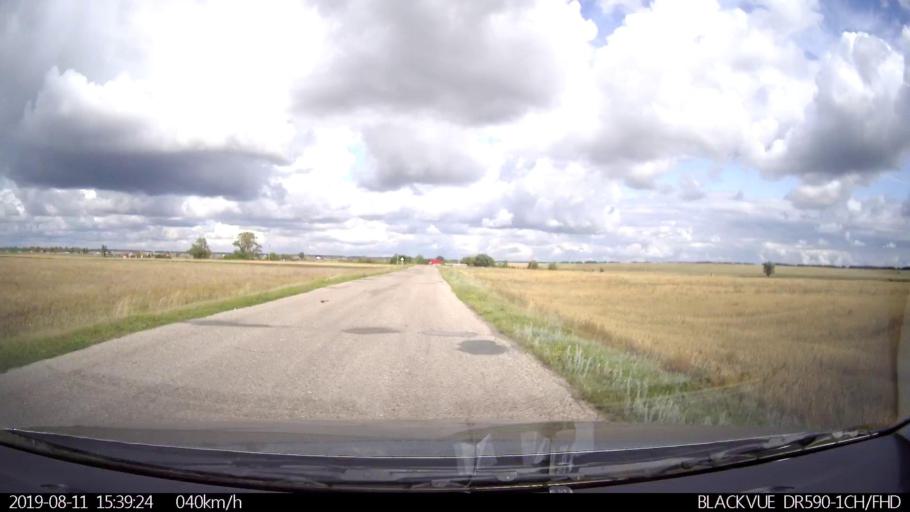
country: RU
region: Ulyanovsk
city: Ignatovka
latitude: 53.8674
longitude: 47.6411
